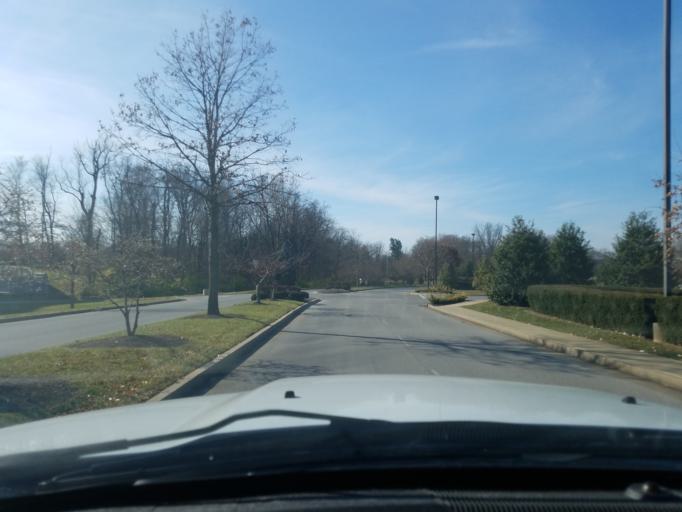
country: US
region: Kentucky
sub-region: Jefferson County
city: Douglass Hills
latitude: 38.2268
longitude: -85.5480
